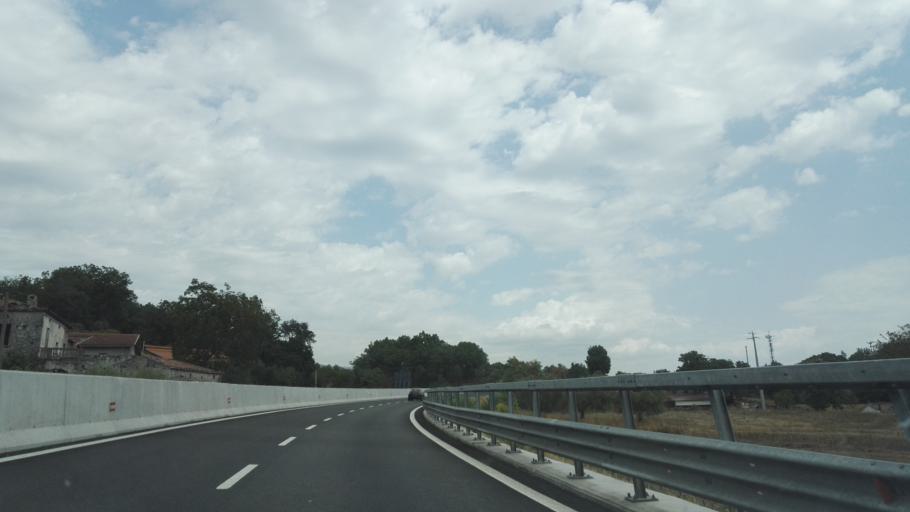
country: IT
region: Calabria
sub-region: Provincia di Cosenza
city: Laino Borgo
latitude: 39.9691
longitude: 15.9327
